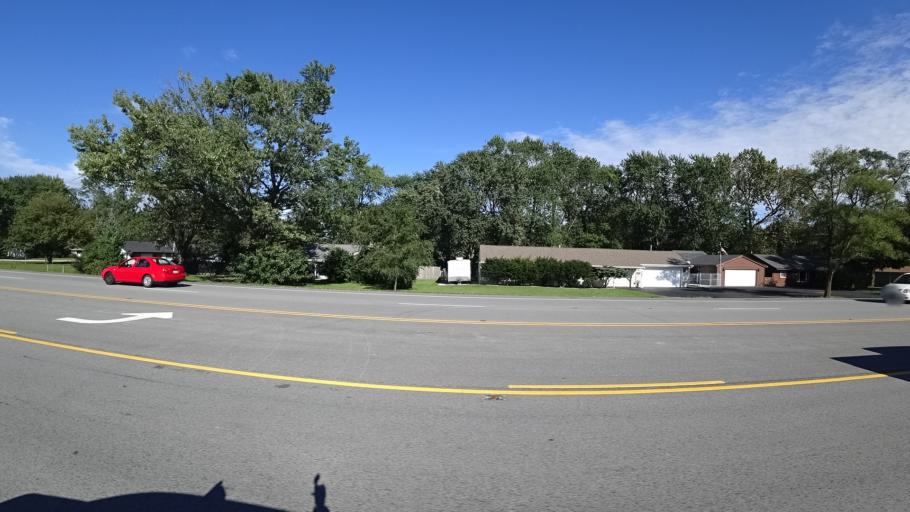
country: US
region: Illinois
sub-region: Cook County
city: Country Club Hills
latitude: 41.5603
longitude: -87.7333
